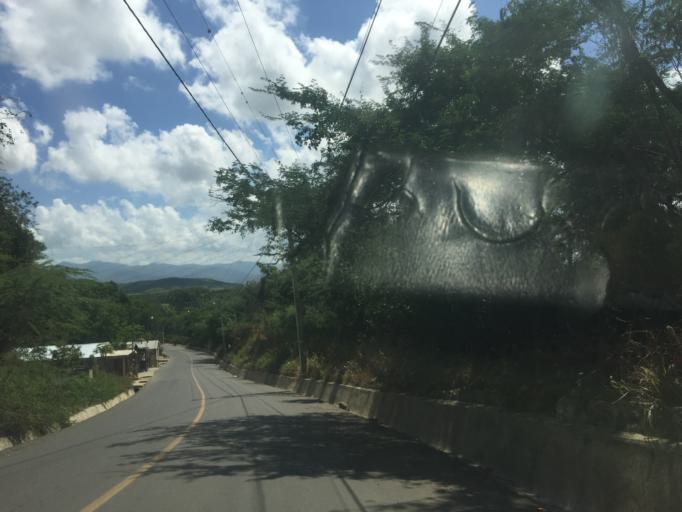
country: DO
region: Santiago
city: Santiago de los Caballeros
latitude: 19.4479
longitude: -70.7546
